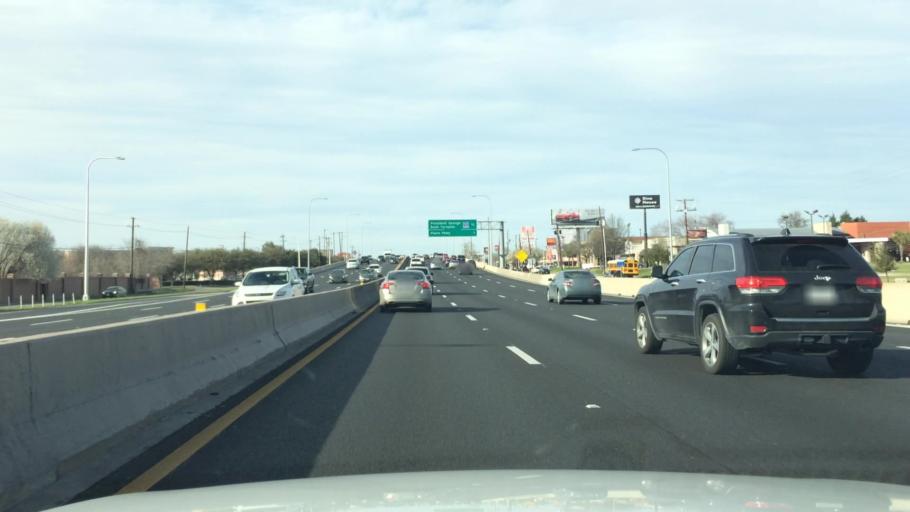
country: US
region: Texas
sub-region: Dallas County
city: Addison
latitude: 32.9939
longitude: -96.8294
